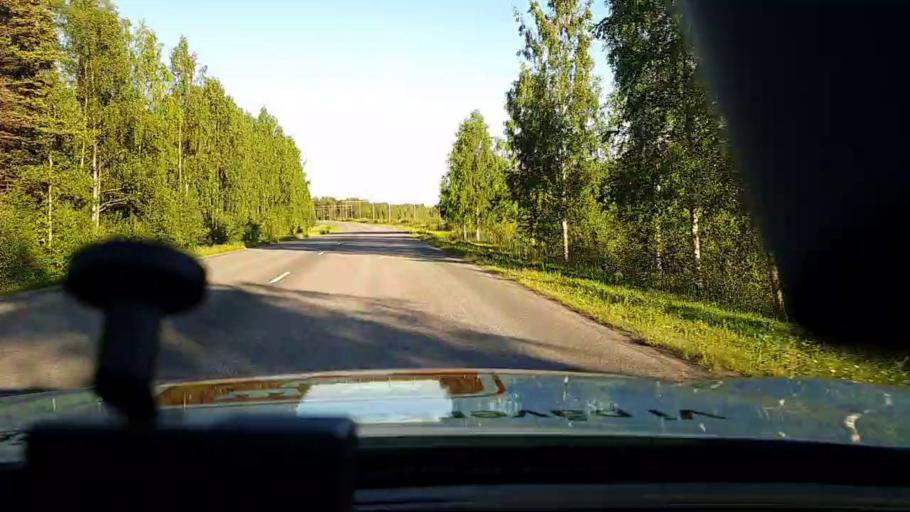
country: SE
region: Norrbotten
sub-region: Lulea Kommun
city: Lulea
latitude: 65.6104
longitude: 22.1650
